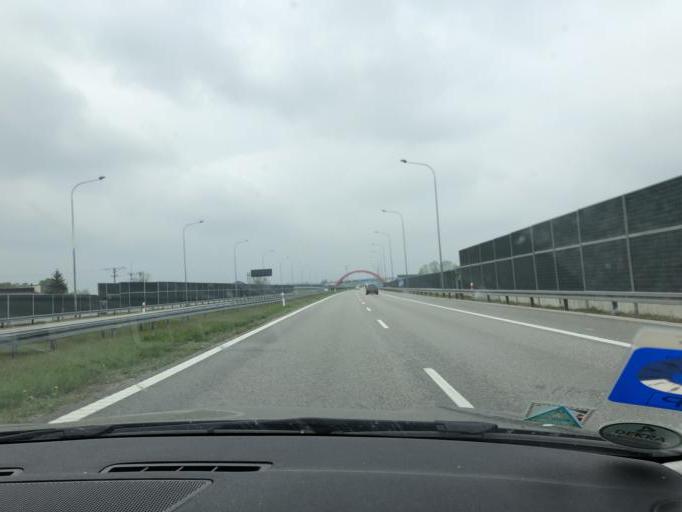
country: PL
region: Subcarpathian Voivodeship
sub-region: Powiat debicki
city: Zyrakow
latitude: 50.0796
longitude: 21.3933
